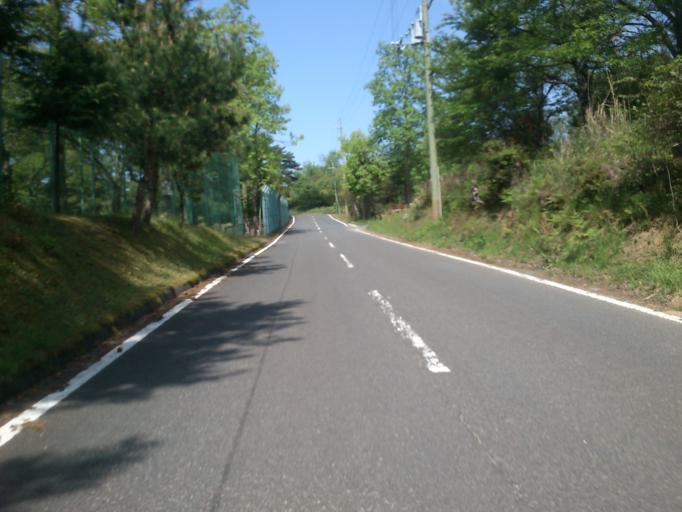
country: JP
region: Kyoto
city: Miyazu
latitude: 35.6268
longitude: 135.2239
